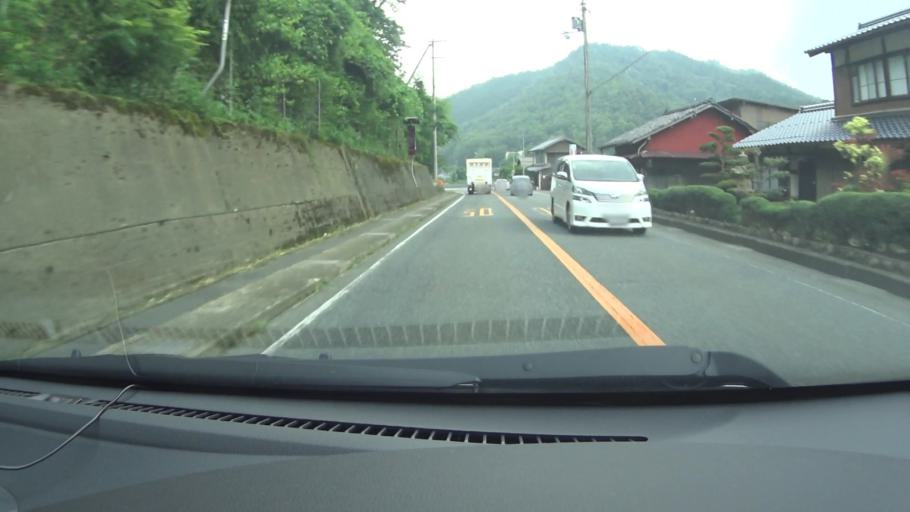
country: JP
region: Kyoto
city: Ayabe
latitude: 35.3540
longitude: 135.3119
